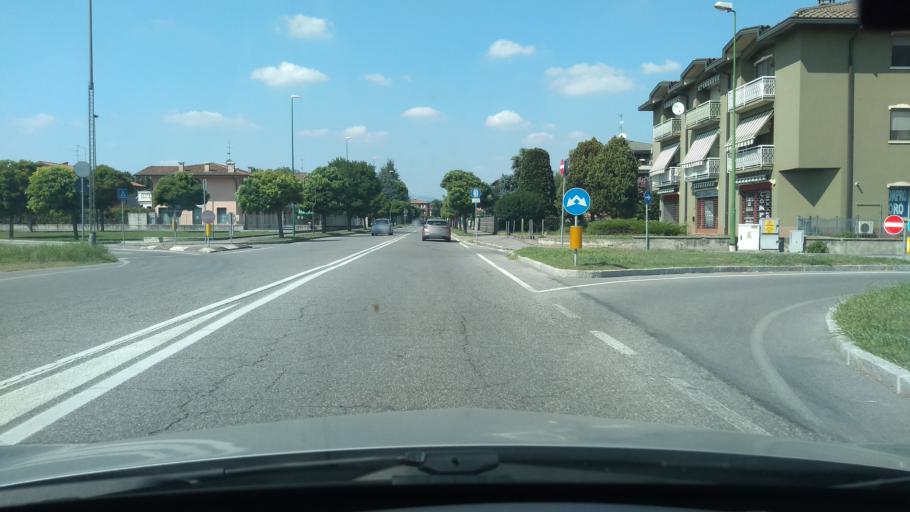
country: IT
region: Lombardy
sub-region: Provincia di Bergamo
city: Ghisalba
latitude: 45.5908
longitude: 9.7581
